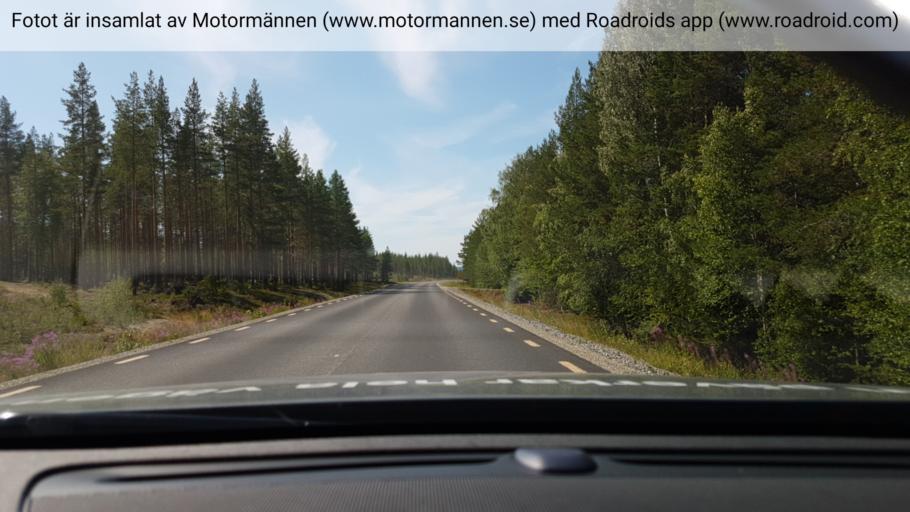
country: SE
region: Vaesterbotten
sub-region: Norsjo Kommun
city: Norsjoe
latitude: 64.5064
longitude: 19.3355
